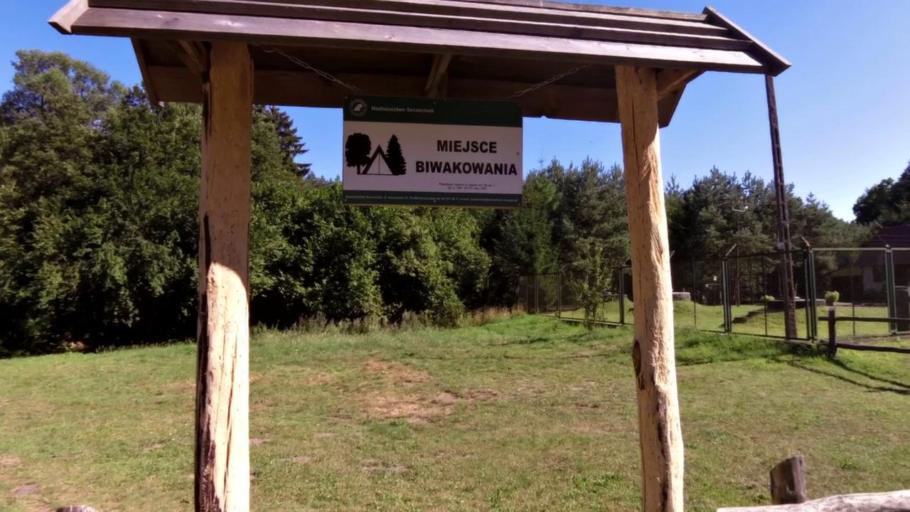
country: PL
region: West Pomeranian Voivodeship
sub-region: Powiat szczecinecki
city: Szczecinek
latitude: 53.7932
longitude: 16.6845
